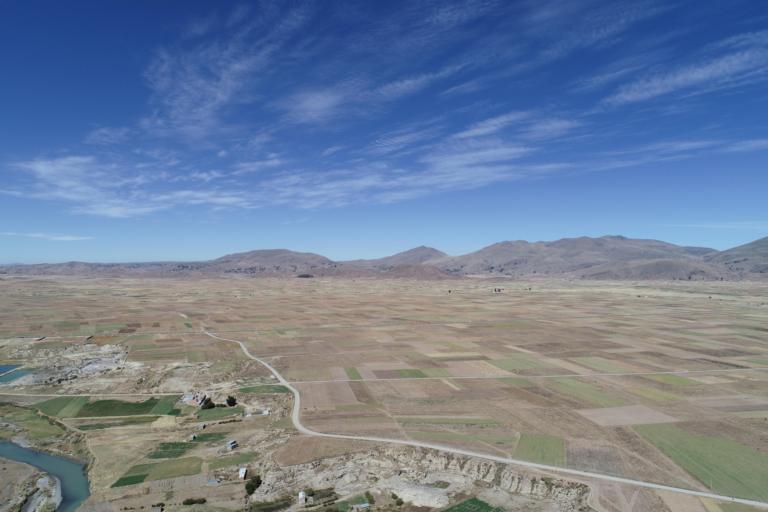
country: BO
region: La Paz
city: Achacachi
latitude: -16.0358
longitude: -68.7018
